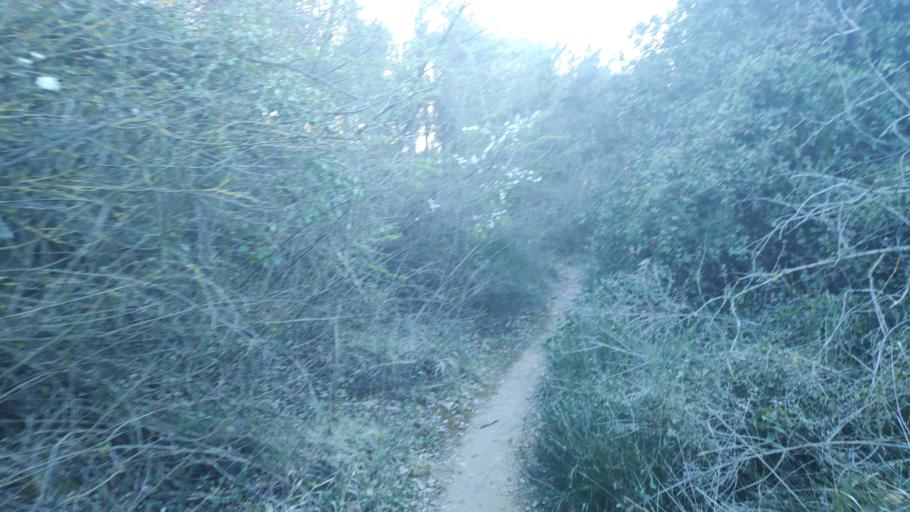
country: ES
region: Catalonia
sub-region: Provincia de Barcelona
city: Sant Quirze del Valles
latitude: 41.5319
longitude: 2.0689
